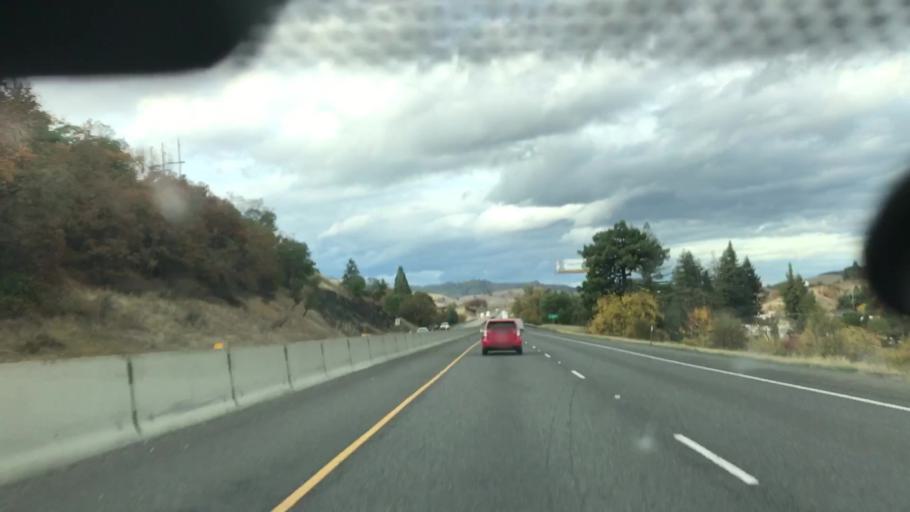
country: US
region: Oregon
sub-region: Douglas County
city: Roseburg North
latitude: 43.2774
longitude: -123.3554
